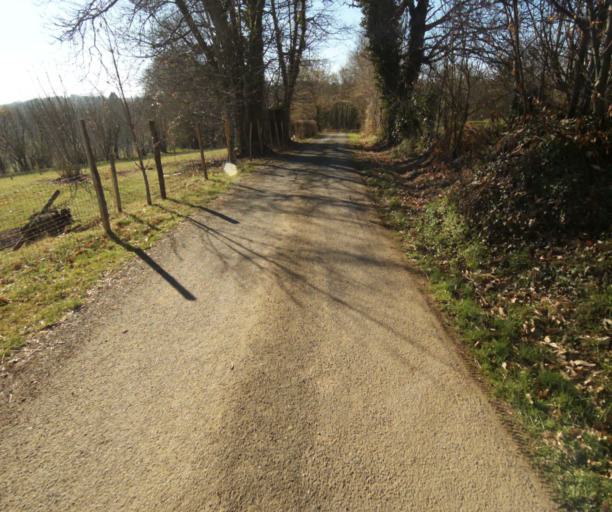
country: FR
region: Limousin
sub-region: Departement de la Correze
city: Chamboulive
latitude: 45.4183
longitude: 1.6829
